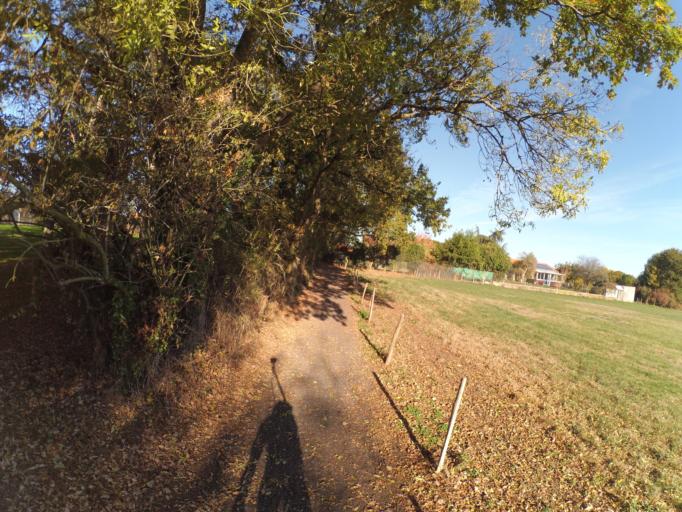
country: FR
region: Pays de la Loire
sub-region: Departement de la Loire-Atlantique
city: Saint-Lumine-de-Clisson
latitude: 47.0842
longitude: -1.3333
